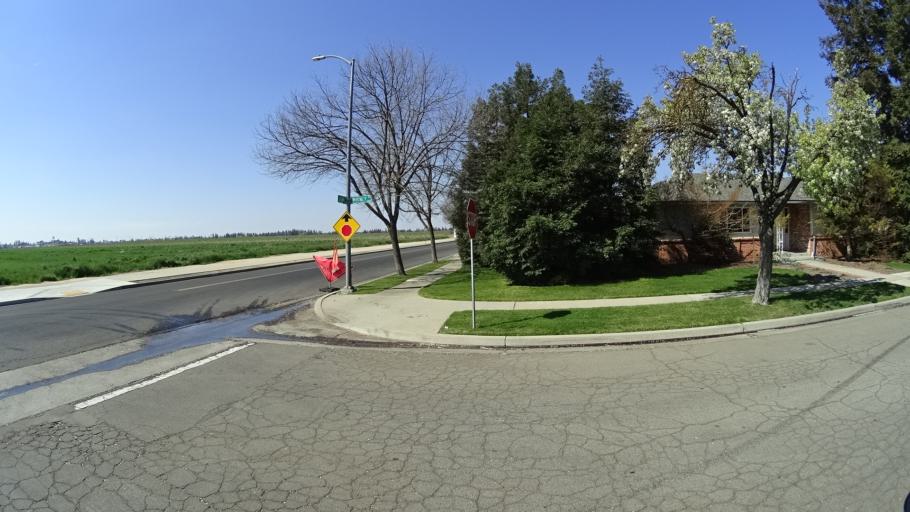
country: US
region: California
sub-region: Fresno County
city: Clovis
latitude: 36.8304
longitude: -119.7391
